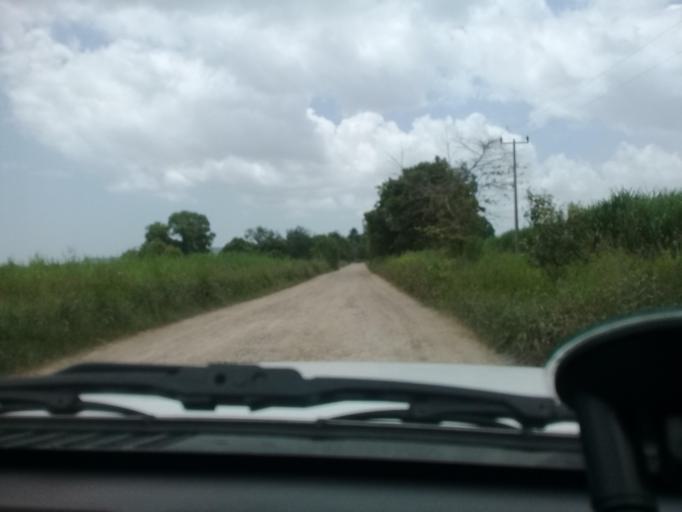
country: MX
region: Veracruz
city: Panuco
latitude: 22.1293
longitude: -98.0617
